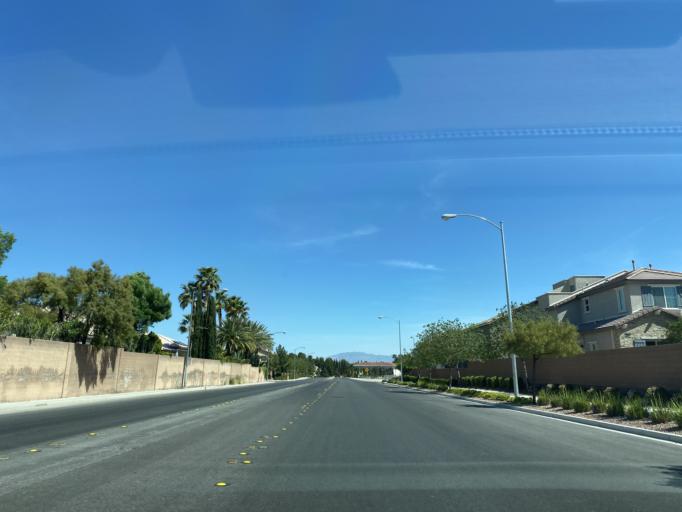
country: US
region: Nevada
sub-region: Clark County
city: Spring Valley
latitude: 36.0892
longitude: -115.2610
